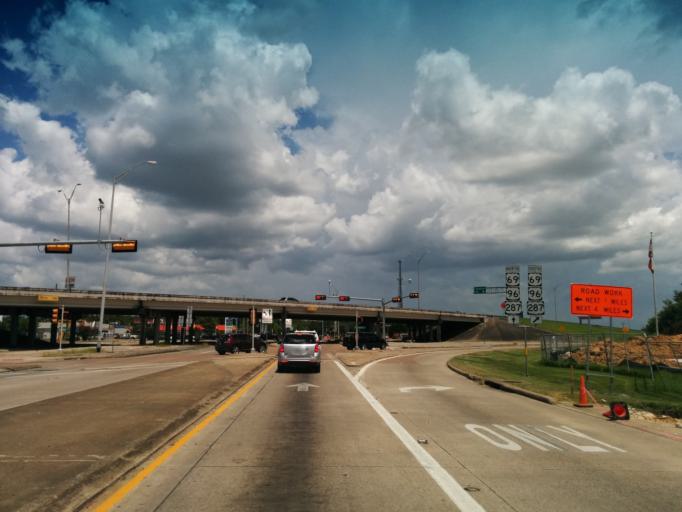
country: US
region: Texas
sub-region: Jefferson County
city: Beaumont
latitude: 30.1334
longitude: -94.1686
